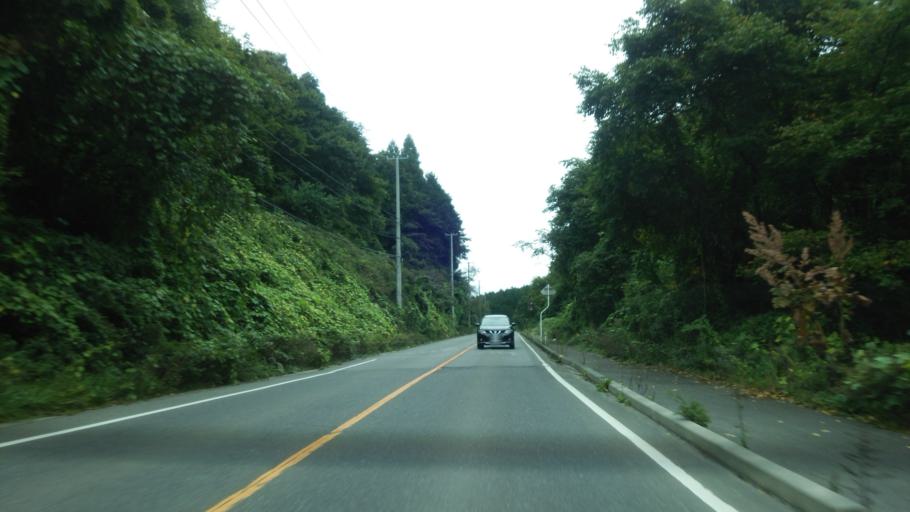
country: JP
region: Fukushima
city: Sukagawa
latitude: 37.1609
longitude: 140.2170
